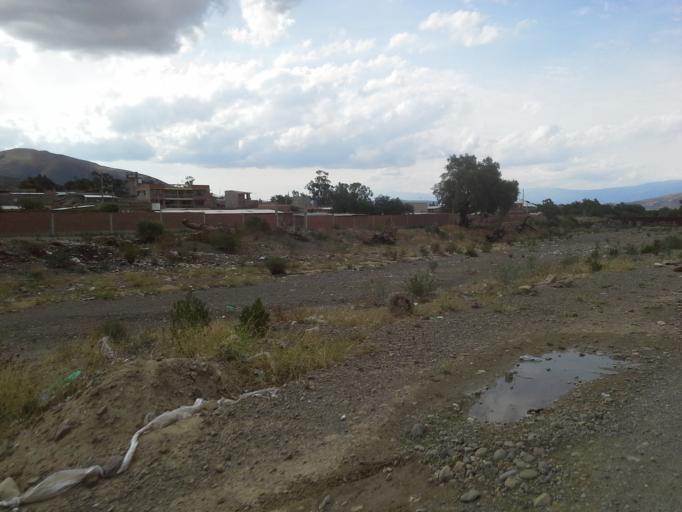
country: BO
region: Cochabamba
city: Tarata
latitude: -17.6098
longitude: -66.0207
